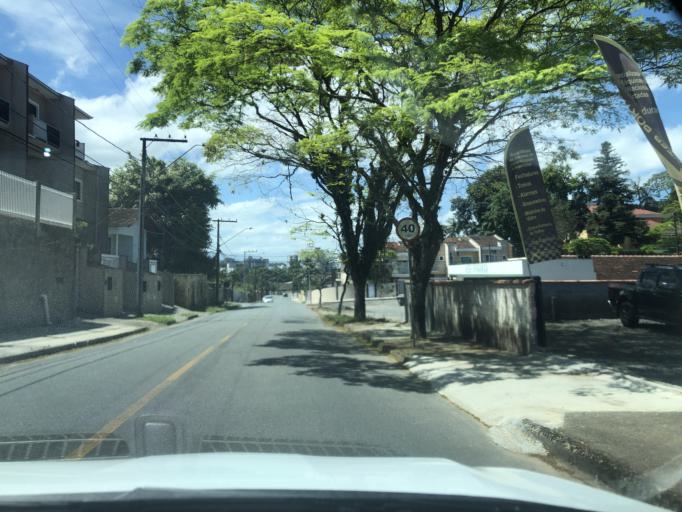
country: BR
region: Santa Catarina
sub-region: Joinville
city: Joinville
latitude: -26.3259
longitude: -48.8522
